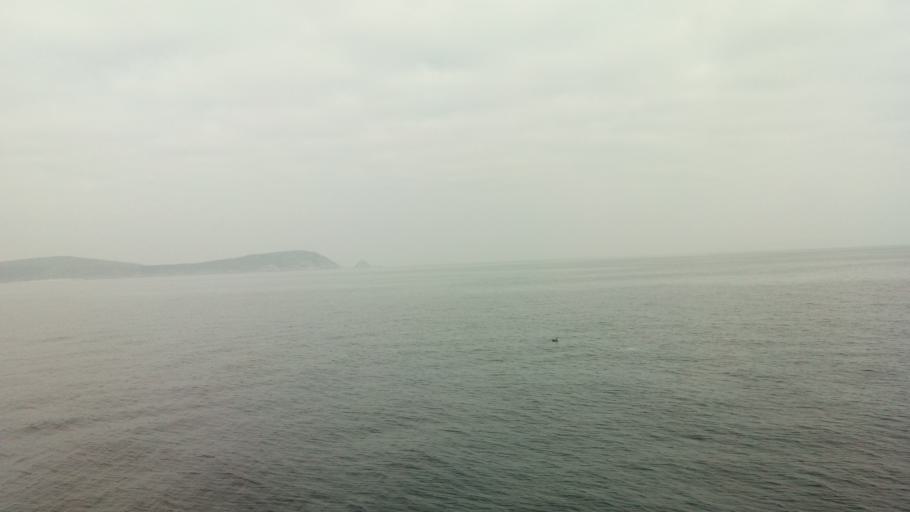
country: ES
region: Galicia
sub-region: Provincia de Pontevedra
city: Sanxenxo
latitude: 42.3796
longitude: -8.8879
